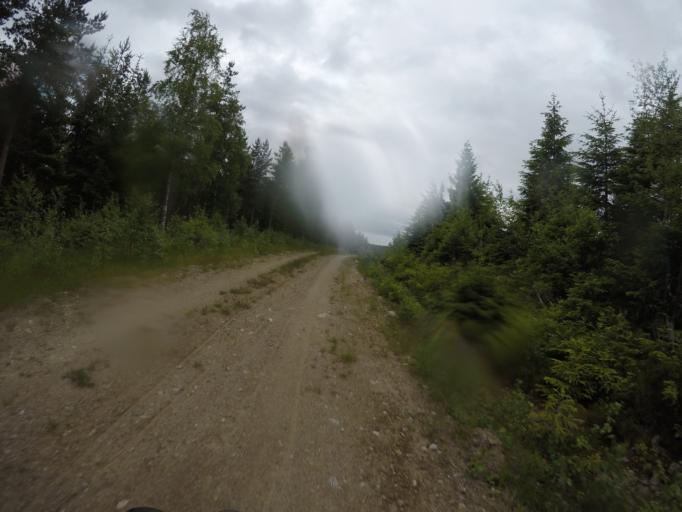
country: SE
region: Dalarna
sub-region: Ludvika Kommun
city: Abborrberget
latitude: 60.0544
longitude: 14.5759
